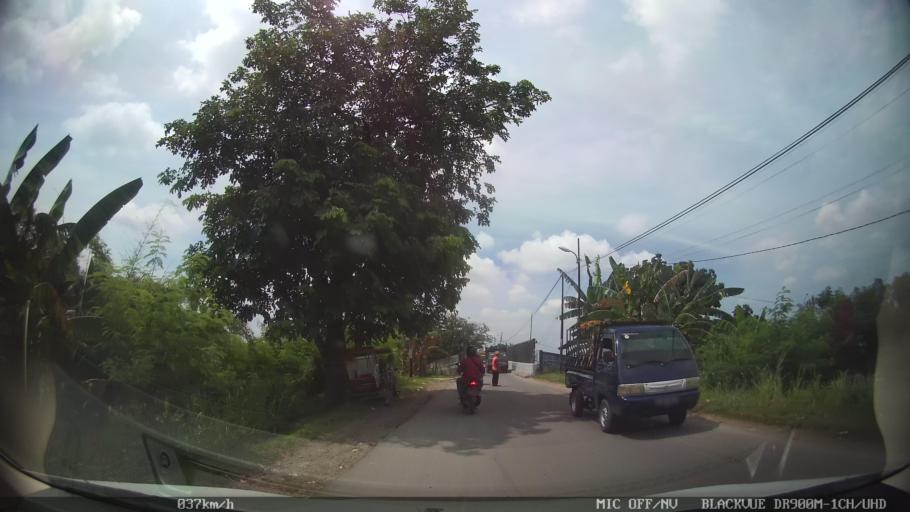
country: ID
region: North Sumatra
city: Medan
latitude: 3.6467
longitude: 98.6876
